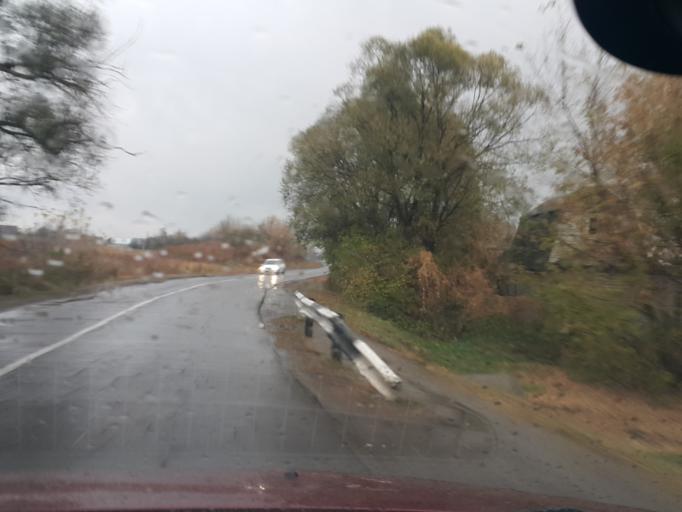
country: RU
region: Tambov
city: Kotovsk
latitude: 52.5390
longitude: 41.4765
